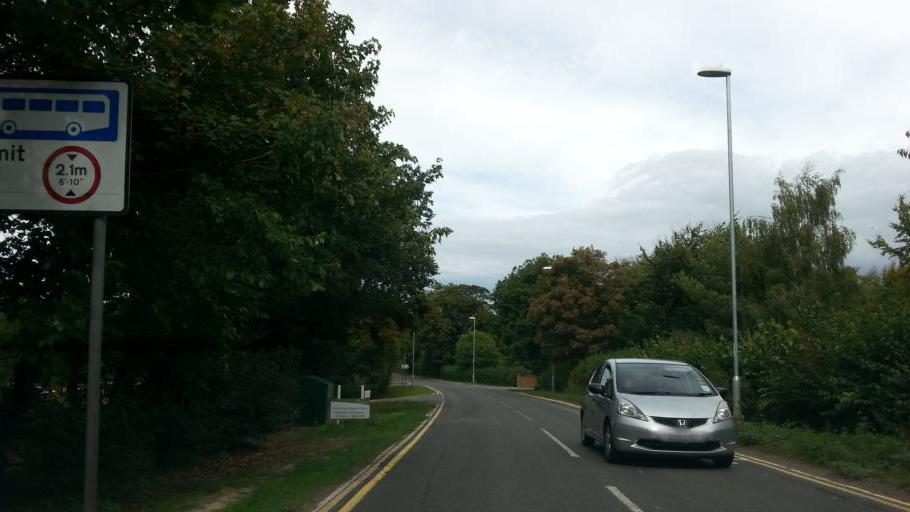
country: GB
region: England
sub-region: Cambridgeshire
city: Sawston
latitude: 52.1673
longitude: 0.1623
